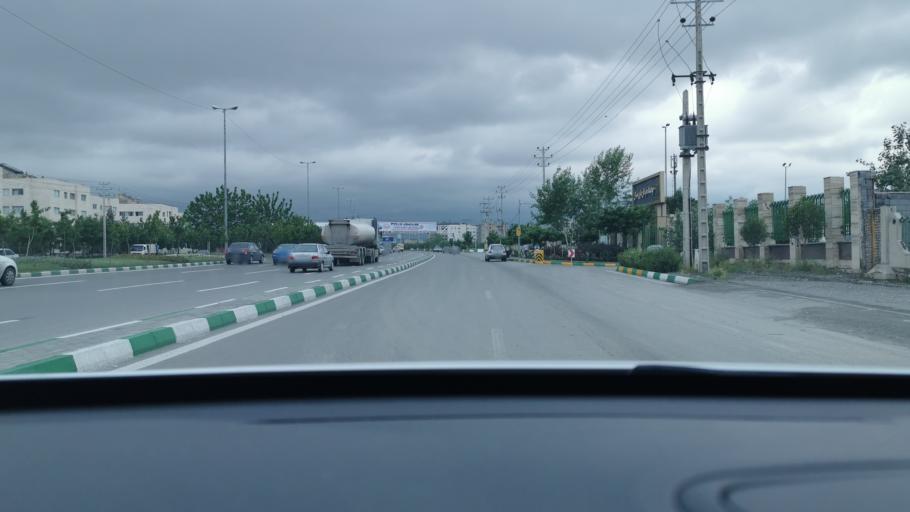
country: IR
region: Razavi Khorasan
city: Mashhad
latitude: 36.3770
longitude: 59.5069
